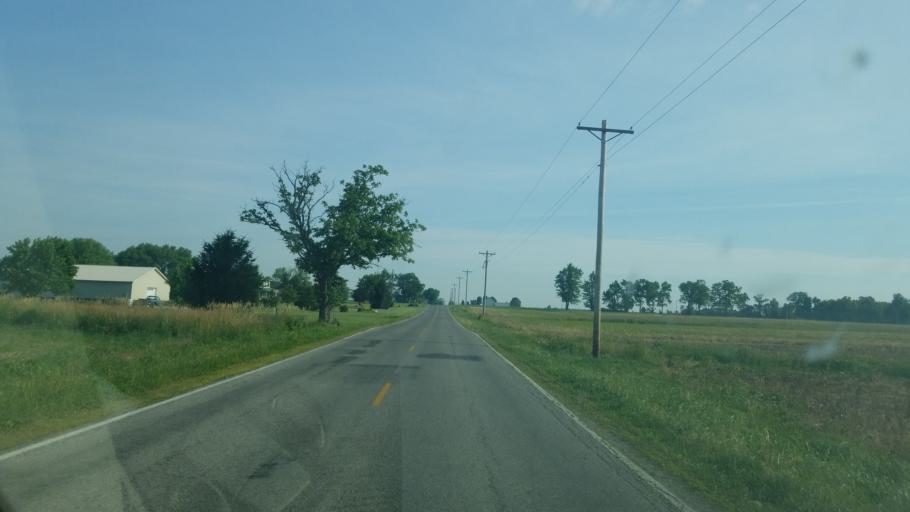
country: US
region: Ohio
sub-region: Hancock County
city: Arlington
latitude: 40.9465
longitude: -83.6987
